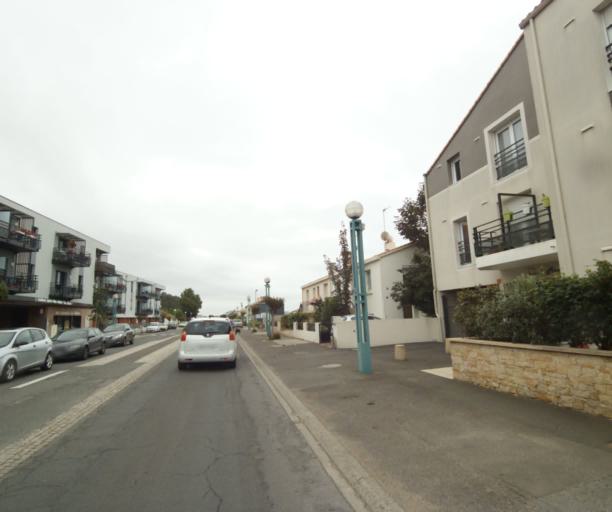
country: FR
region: Pays de la Loire
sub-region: Departement de la Vendee
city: Chateau-d'Olonne
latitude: 46.4913
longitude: -1.7564
